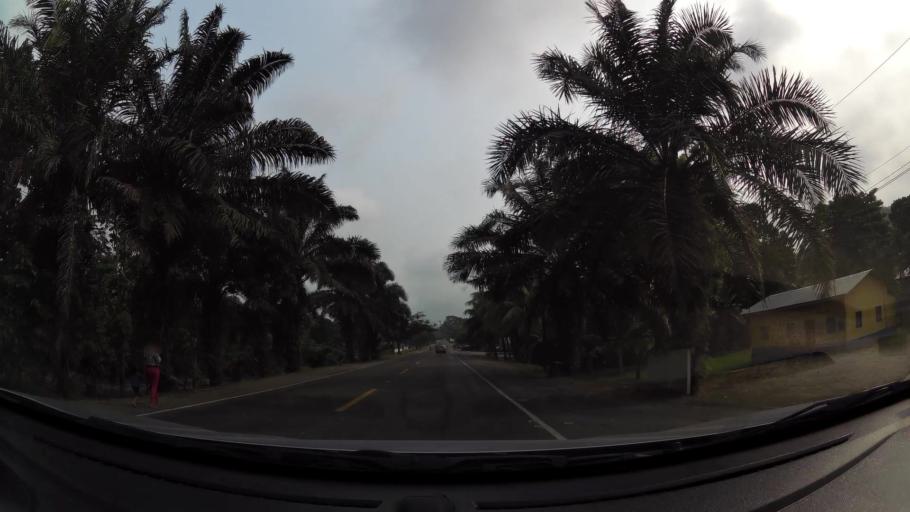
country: HN
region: Yoro
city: Toyos
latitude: 15.5462
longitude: -87.6518
